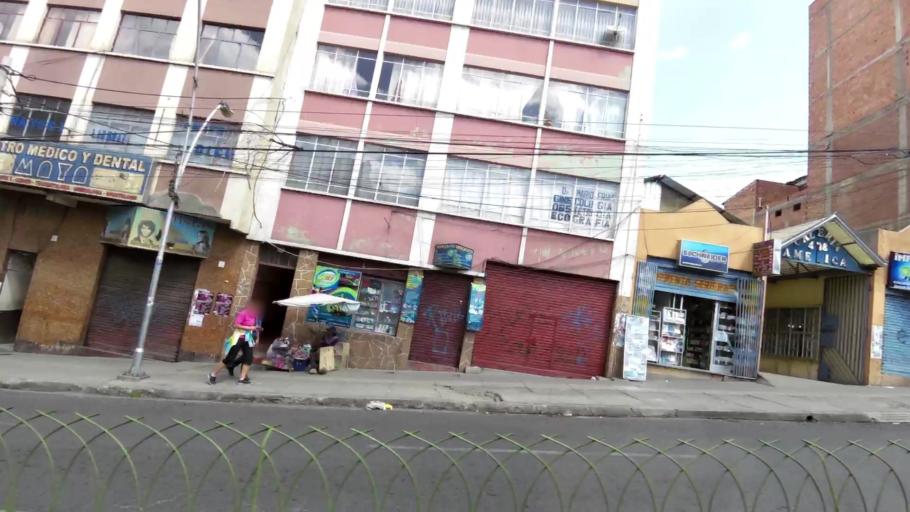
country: BO
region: La Paz
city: La Paz
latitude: -16.4933
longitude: -68.1417
